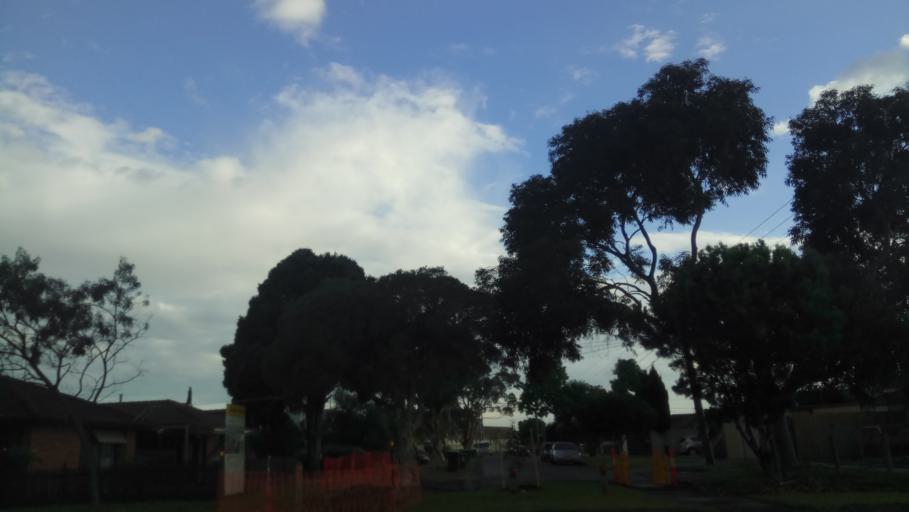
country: AU
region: Victoria
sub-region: Hobsons Bay
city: Laverton
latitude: -37.8667
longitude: 144.7759
